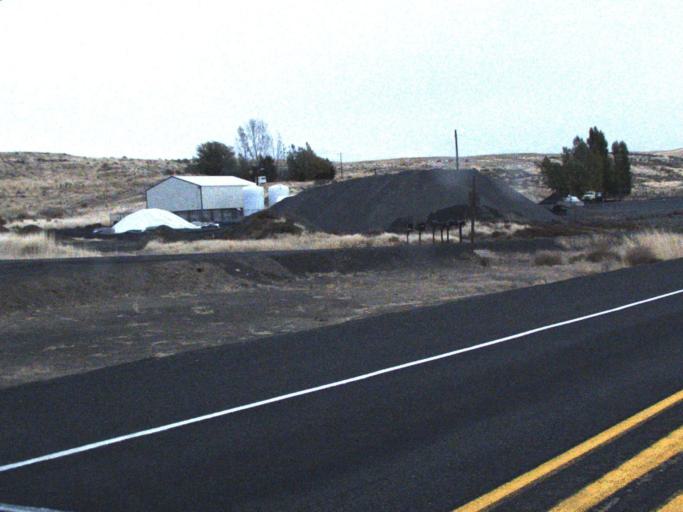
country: US
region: Washington
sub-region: Adams County
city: Ritzville
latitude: 46.7586
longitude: -118.3110
